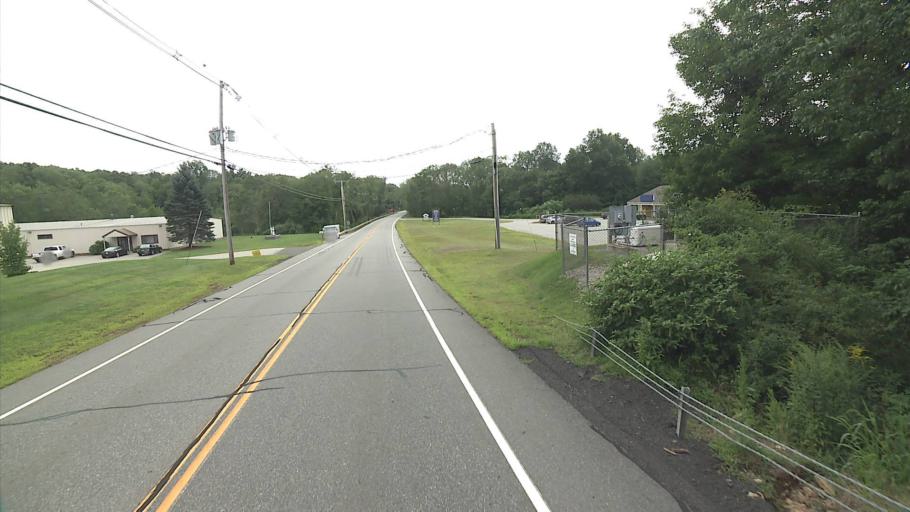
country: US
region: Connecticut
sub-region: Tolland County
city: Storrs
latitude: 41.8630
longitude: -72.1885
